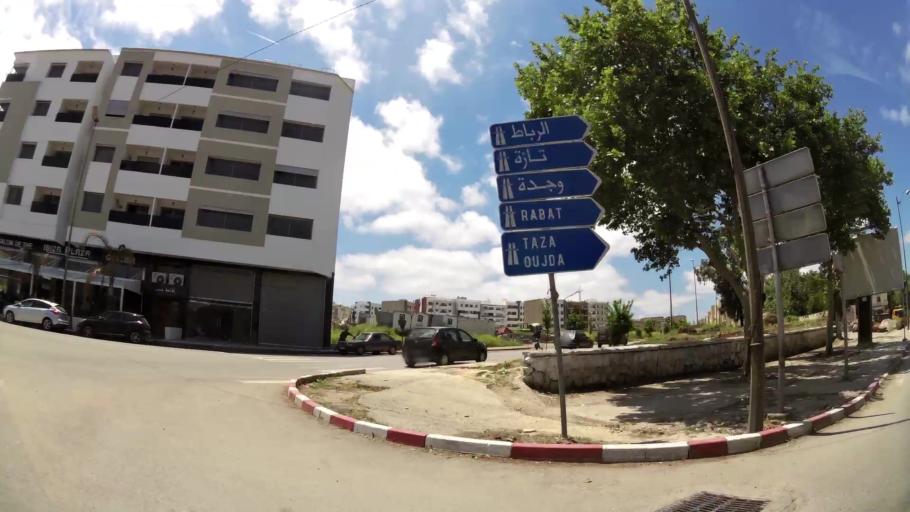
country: MA
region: Fes-Boulemane
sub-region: Fes
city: Fes
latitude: 34.0406
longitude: -5.0152
